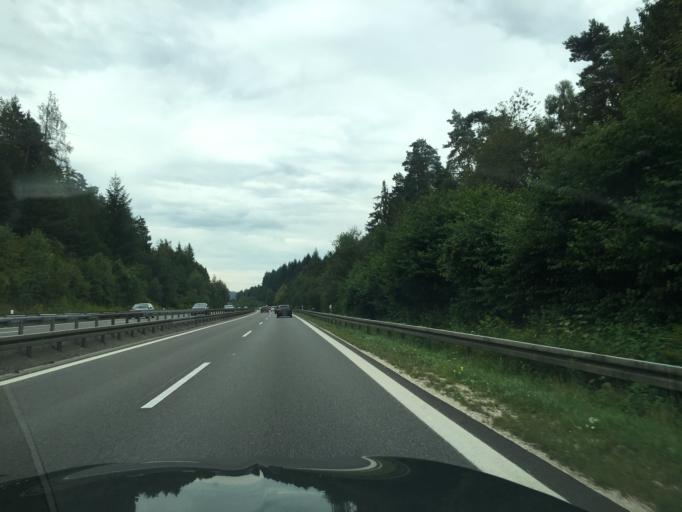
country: DE
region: Baden-Wuerttemberg
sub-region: Freiburg Region
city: Radolfzell am Bodensee
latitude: 47.7563
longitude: 8.9945
